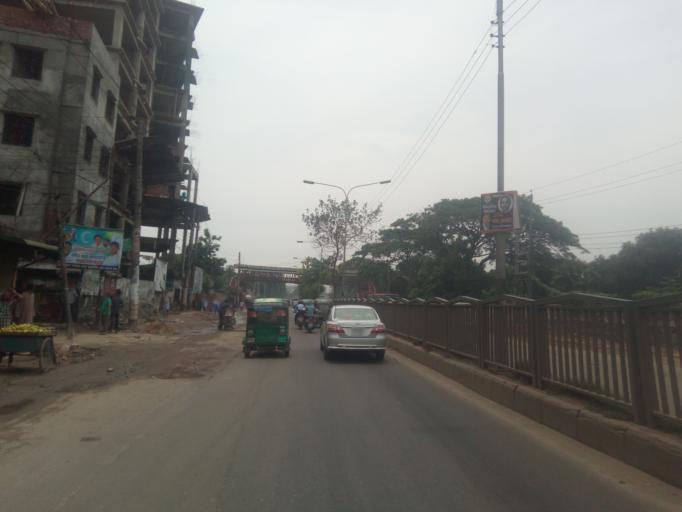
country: BD
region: Dhaka
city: Azimpur
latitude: 23.7798
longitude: 90.3550
